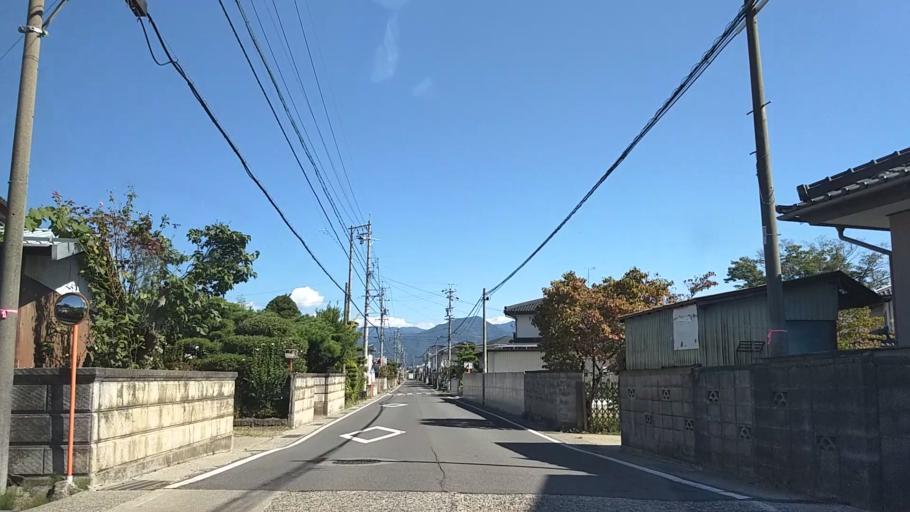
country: JP
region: Nagano
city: Nagano-shi
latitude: 36.6123
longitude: 138.1569
